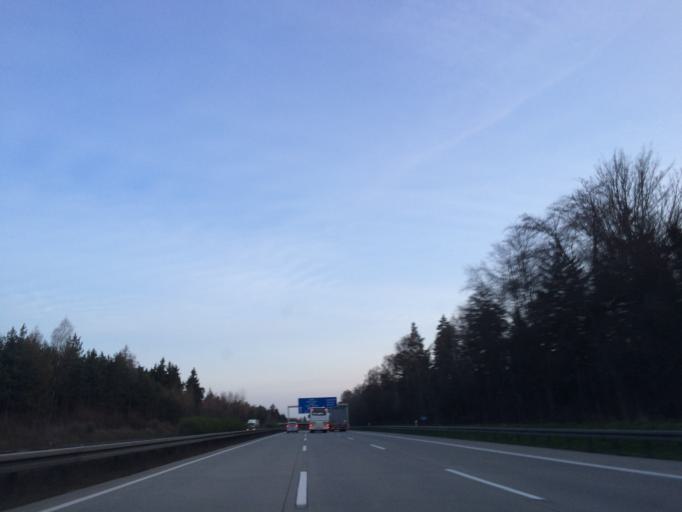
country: DE
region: Thuringia
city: Eineborn
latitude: 50.8529
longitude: 11.8577
